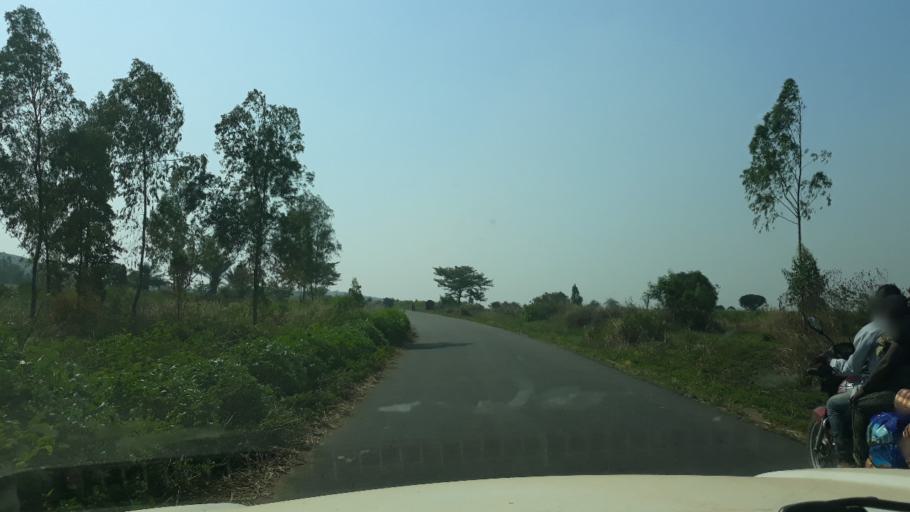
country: CD
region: South Kivu
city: Uvira
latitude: -3.2100
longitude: 29.1642
